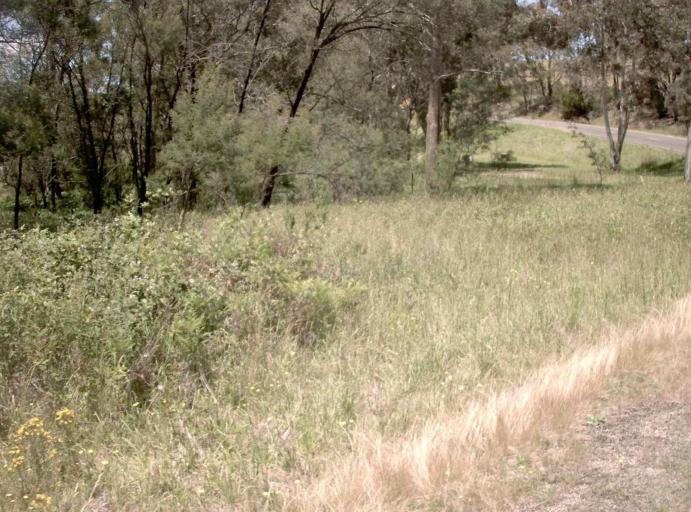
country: AU
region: Victoria
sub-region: East Gippsland
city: Bairnsdale
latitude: -37.4040
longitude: 147.8346
